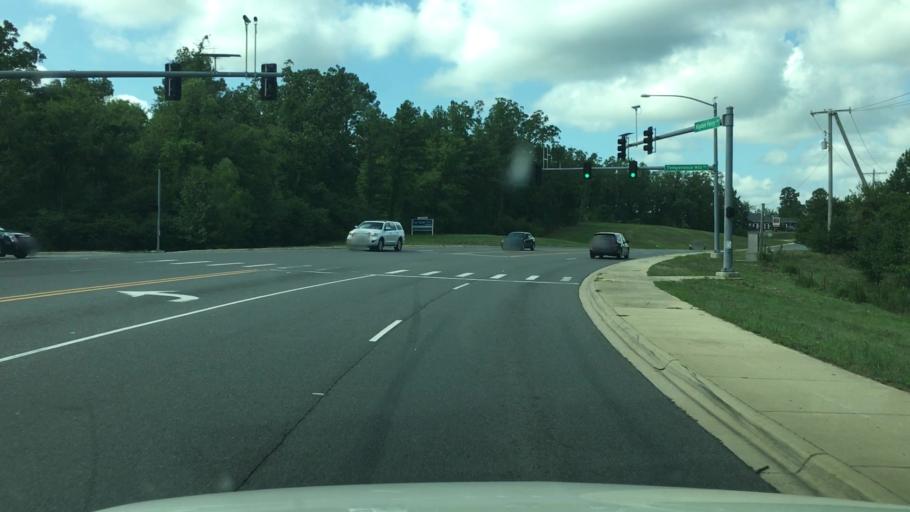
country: US
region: Arkansas
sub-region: Garland County
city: Lake Hamilton
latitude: 34.4548
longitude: -93.0775
